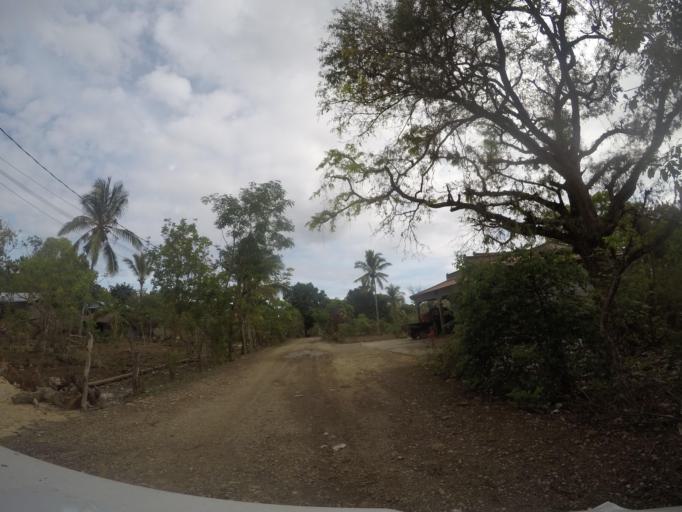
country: TL
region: Baucau
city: Baucau
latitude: -8.4727
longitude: 126.4540
